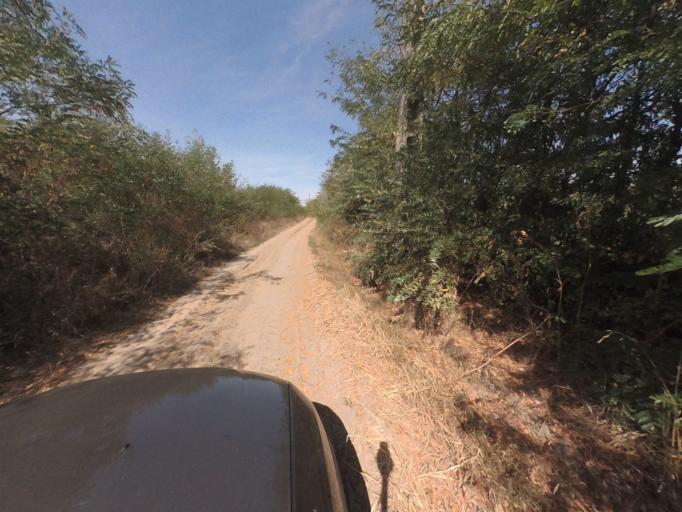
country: RO
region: Vaslui
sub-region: Comuna Costesti
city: Costesti
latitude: 46.5190
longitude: 27.7409
